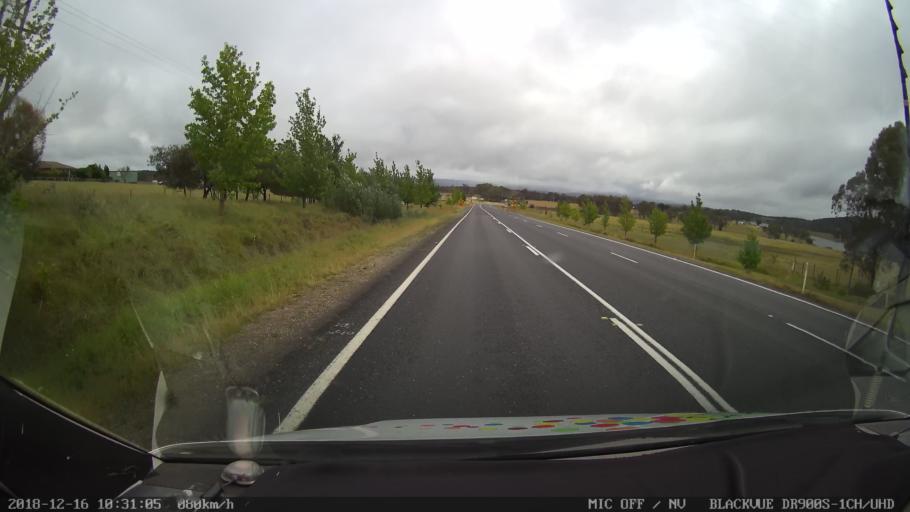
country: AU
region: New South Wales
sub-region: Tenterfield Municipality
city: Carrolls Creek
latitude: -29.0849
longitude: 152.0040
